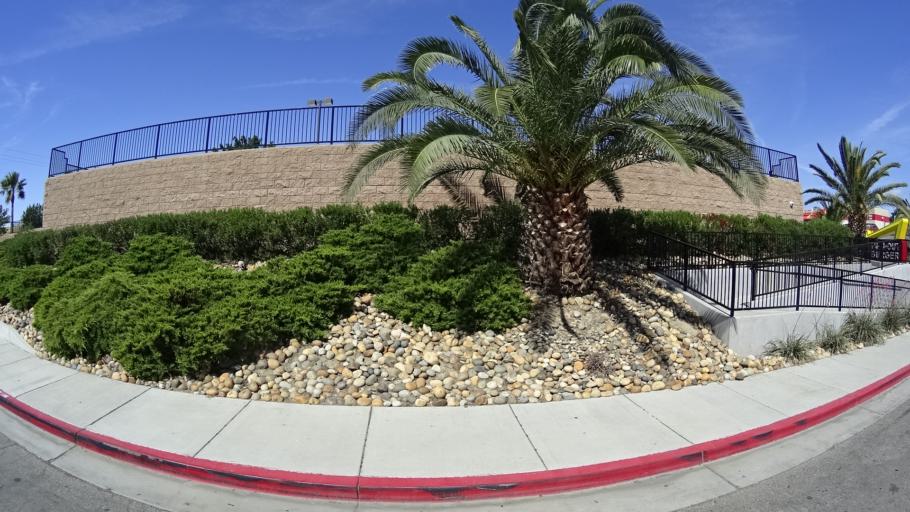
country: US
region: California
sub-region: Kings County
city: Kettleman City
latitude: 35.9861
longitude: -119.9582
